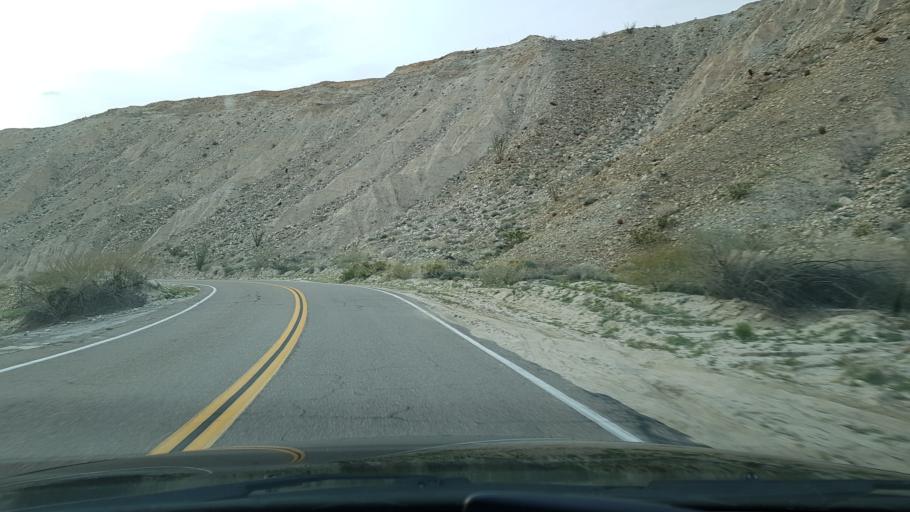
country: US
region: California
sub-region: San Diego County
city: Pine Valley
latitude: 32.8346
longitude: -116.1815
